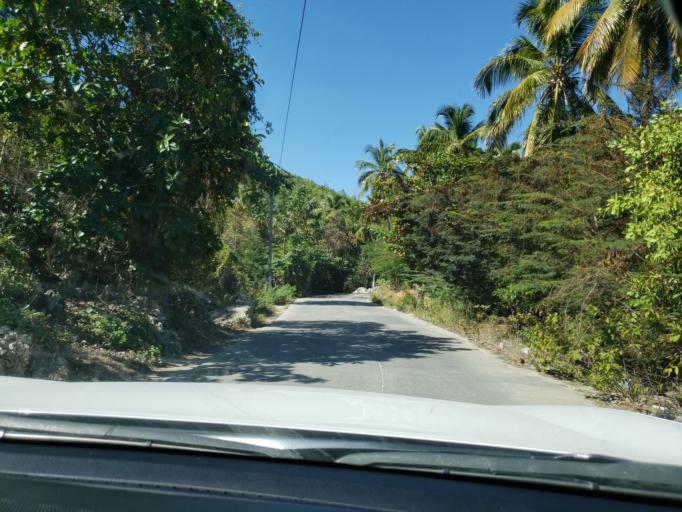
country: HT
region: Nippes
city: Miragoane
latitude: 18.4452
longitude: -73.1040
